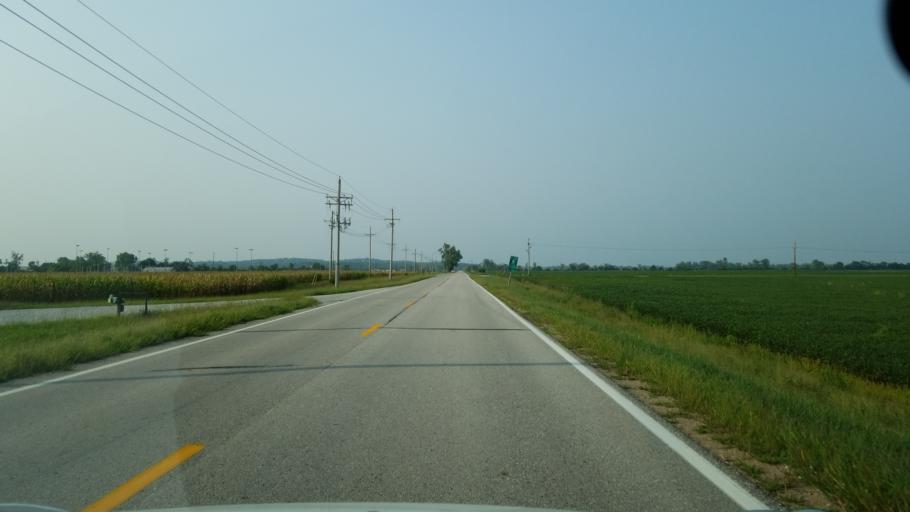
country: US
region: Nebraska
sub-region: Sarpy County
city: Offutt Air Force Base
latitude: 41.0985
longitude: -95.8899
